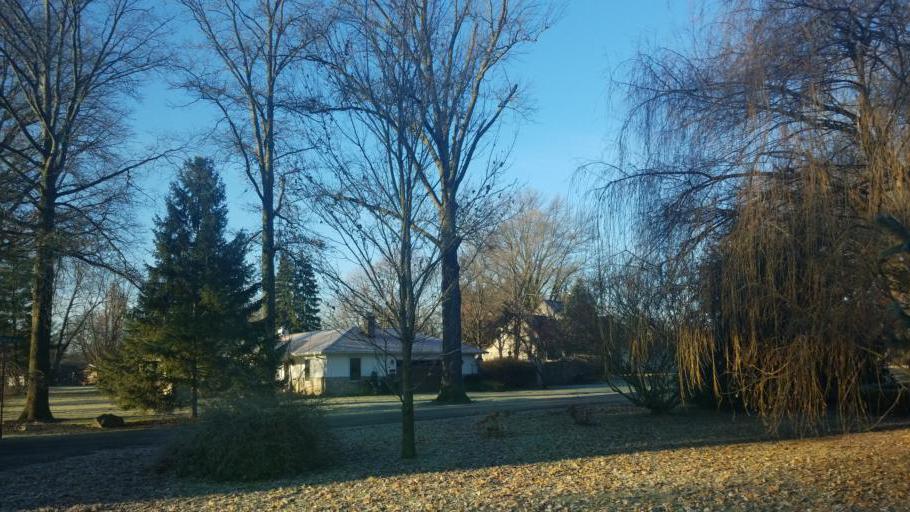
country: US
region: Ohio
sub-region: Marion County
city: Marion
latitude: 40.5762
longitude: -83.1126
